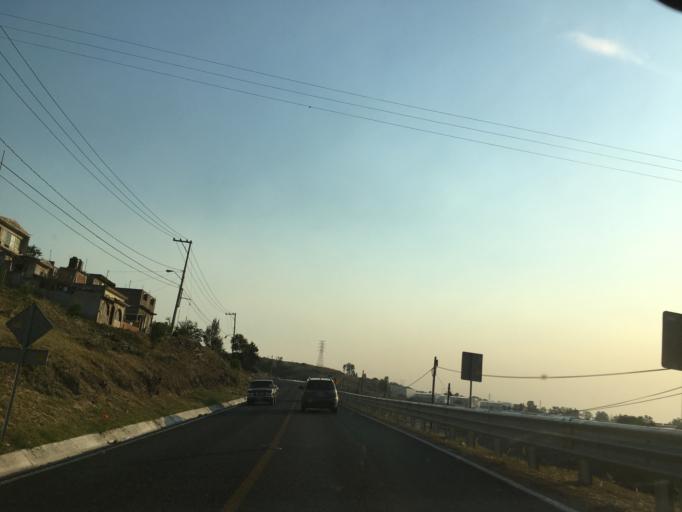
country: MX
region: Michoacan
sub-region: Morelia
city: La Aldea
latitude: 19.7374
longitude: -101.1192
